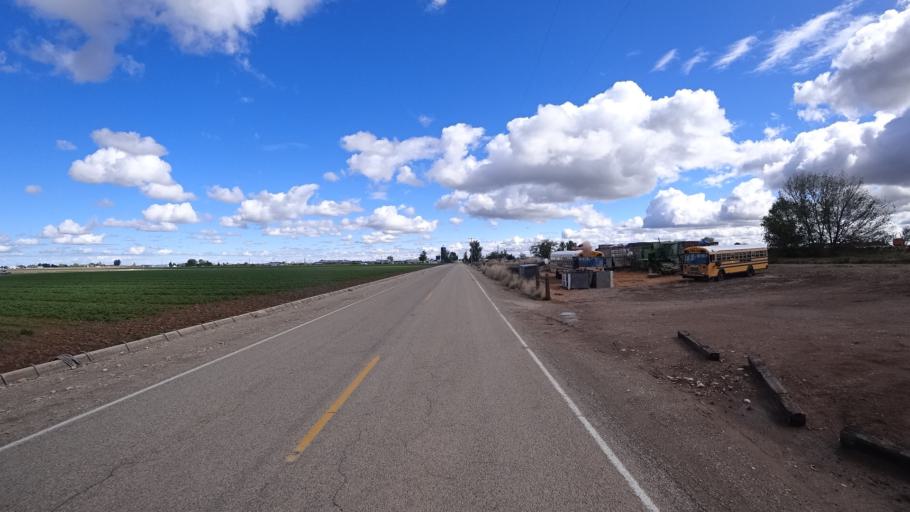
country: US
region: Idaho
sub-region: Ada County
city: Kuna
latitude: 43.4700
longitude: -116.4736
